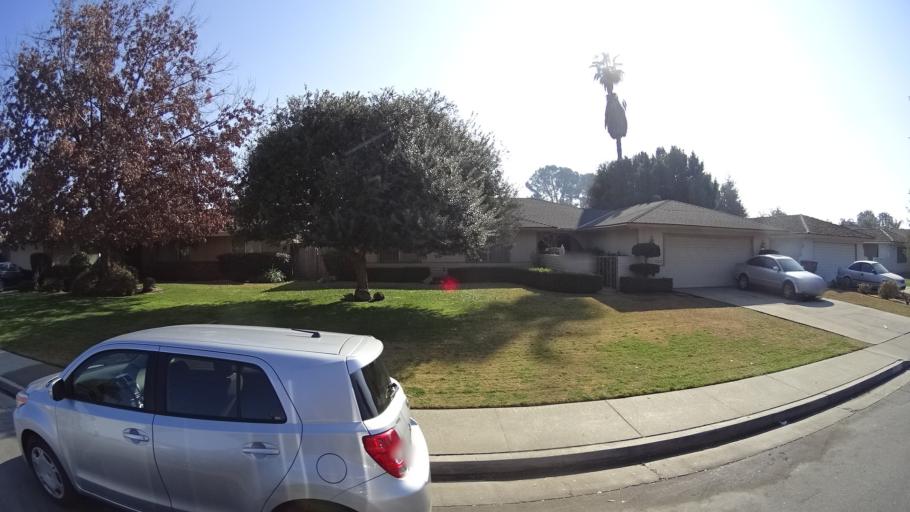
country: US
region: California
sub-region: Kern County
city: Greenacres
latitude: 35.3590
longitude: -119.0703
